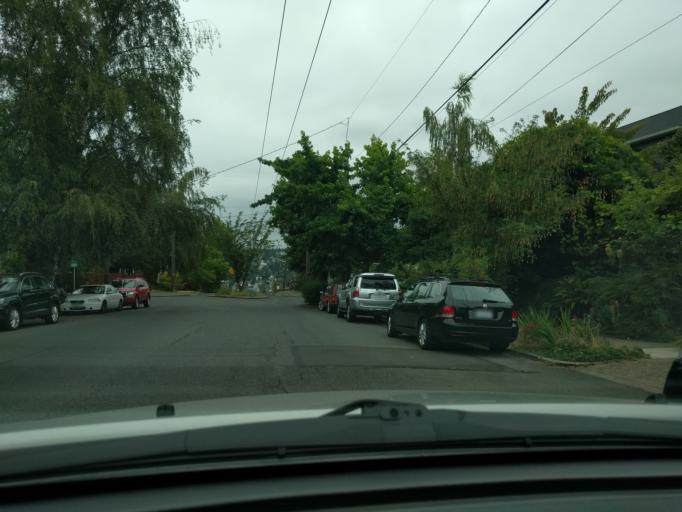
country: US
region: Washington
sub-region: King County
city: Seattle
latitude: 47.6424
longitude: -122.3569
